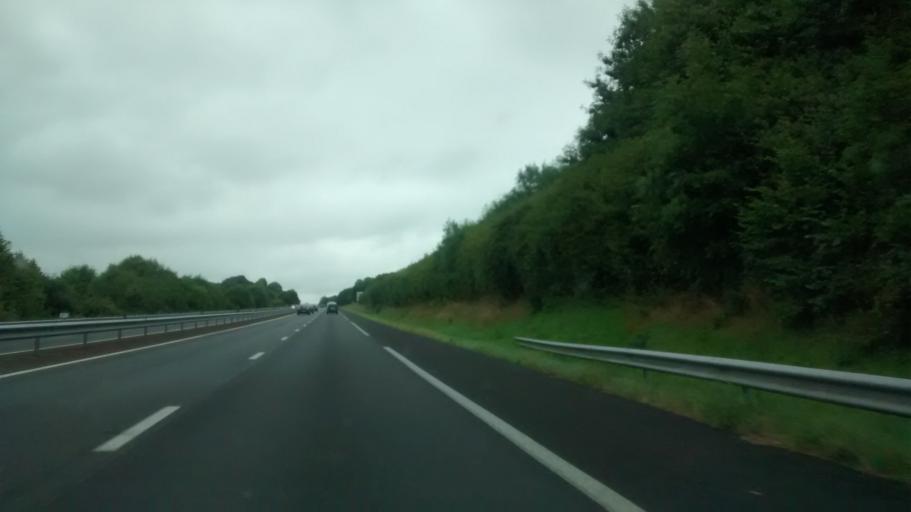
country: FR
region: Lower Normandy
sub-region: Departement de la Manche
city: Villedieu-les-Poeles
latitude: 48.8196
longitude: -1.2503
